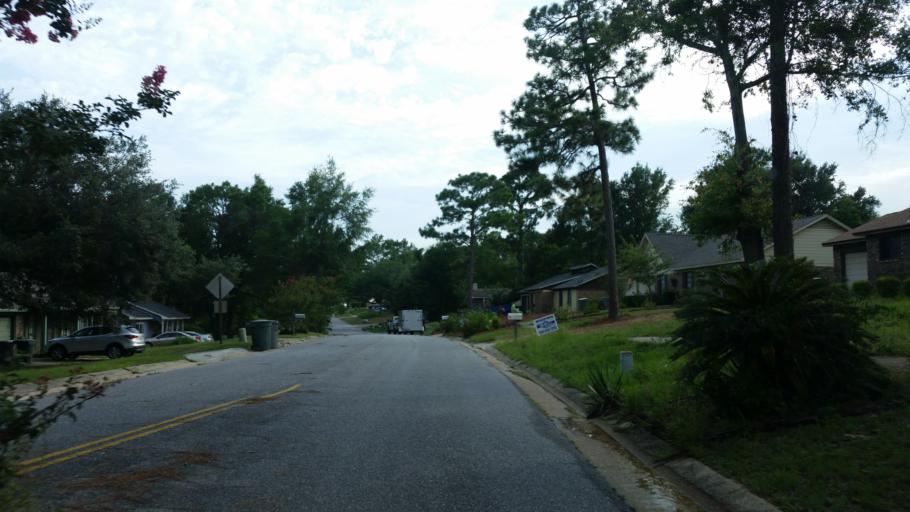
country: US
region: Florida
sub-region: Escambia County
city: Ferry Pass
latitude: 30.5084
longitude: -87.1777
